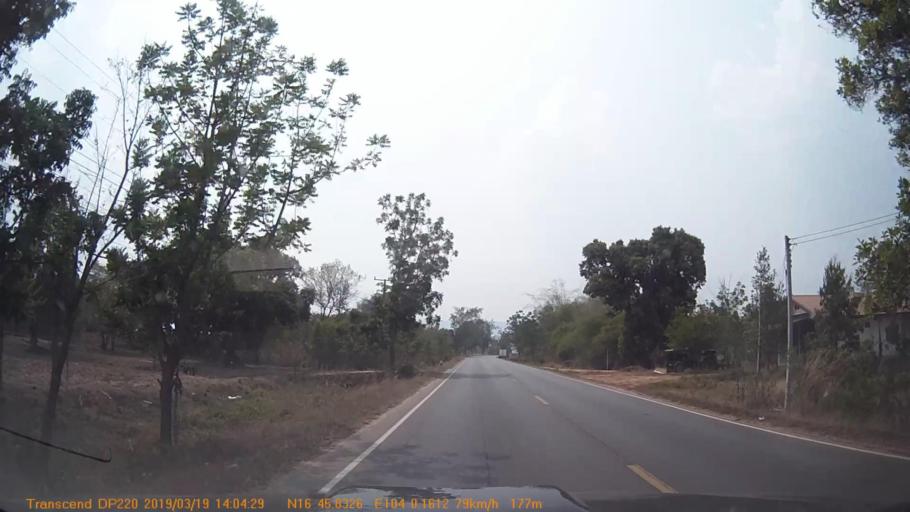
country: TH
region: Kalasin
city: Na Khu
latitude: 16.7640
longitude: 104.0023
